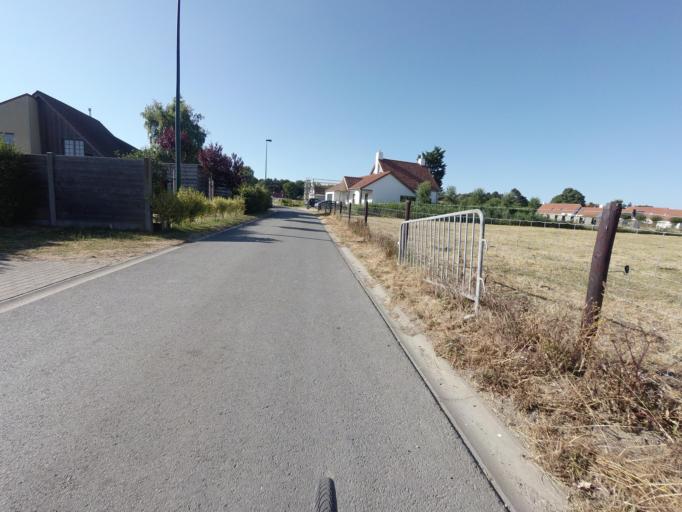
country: BE
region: Flanders
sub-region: Provincie West-Vlaanderen
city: De Haan
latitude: 51.2640
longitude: 3.0166
